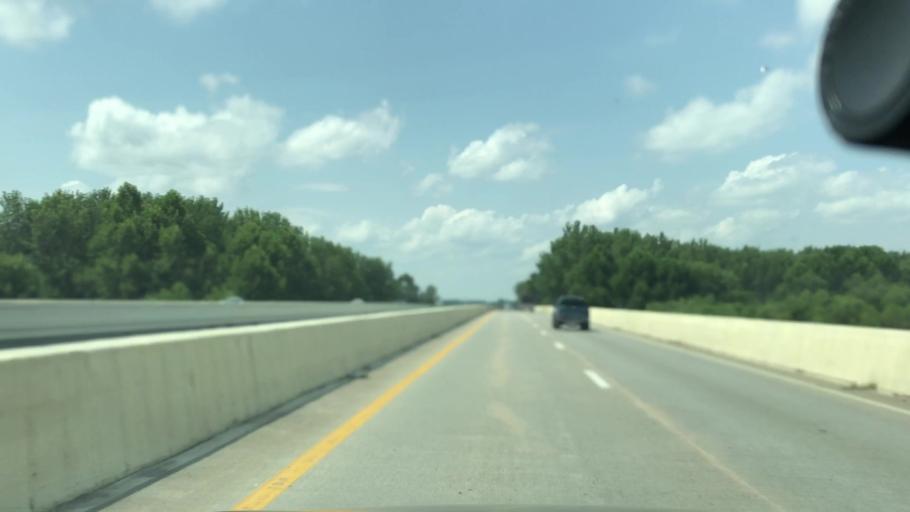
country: US
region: Ohio
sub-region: Ross County
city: Chillicothe
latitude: 39.3057
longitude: -82.9196
